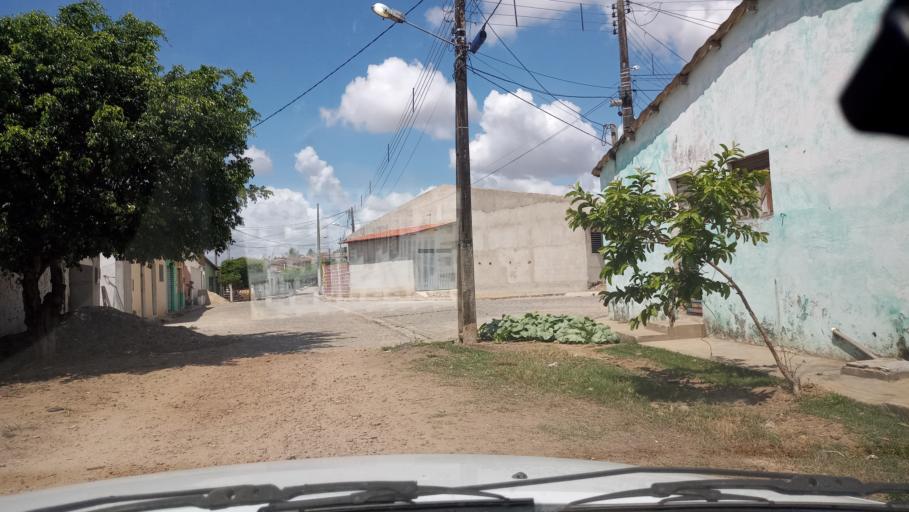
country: BR
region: Rio Grande do Norte
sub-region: Santo Antonio
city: Santo Antonio
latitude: -6.3486
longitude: -35.3729
